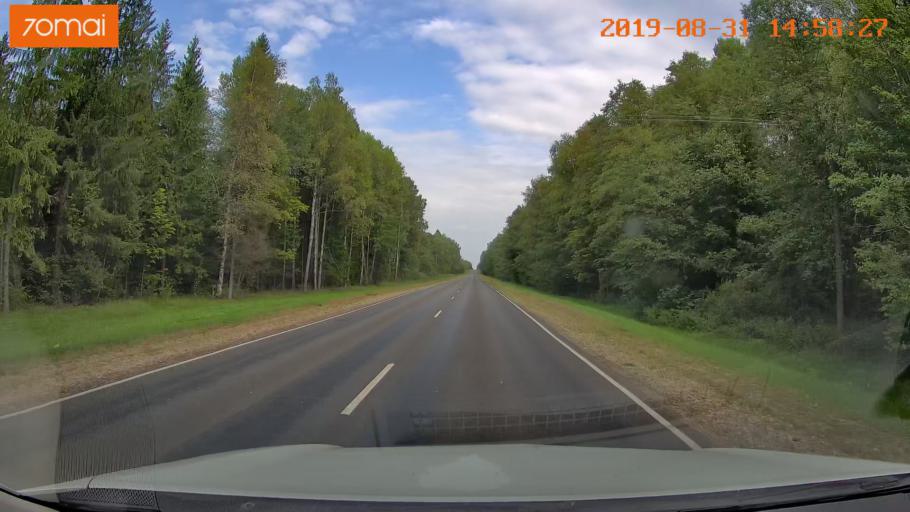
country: RU
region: Kaluga
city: Spas-Demensk
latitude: 54.3177
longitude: 33.9822
